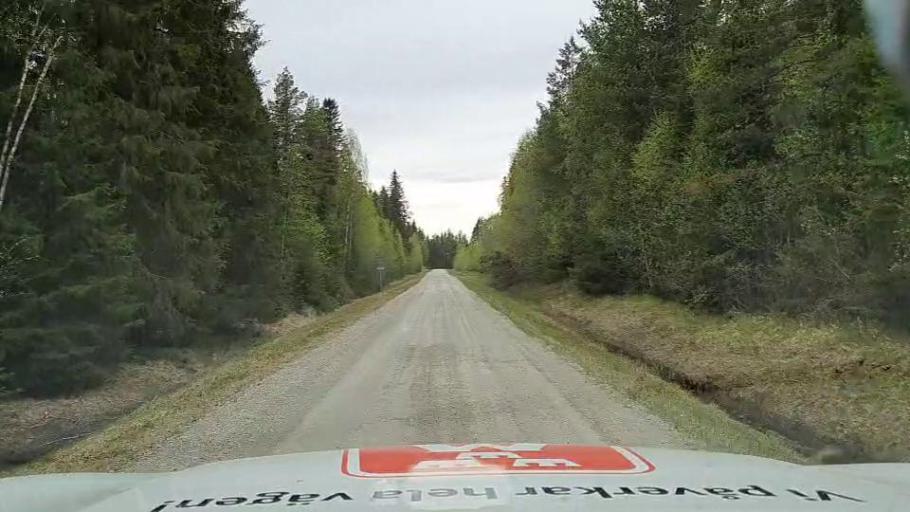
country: SE
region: Jaemtland
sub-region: OEstersunds Kommun
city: Brunflo
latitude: 62.6639
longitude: 14.8343
